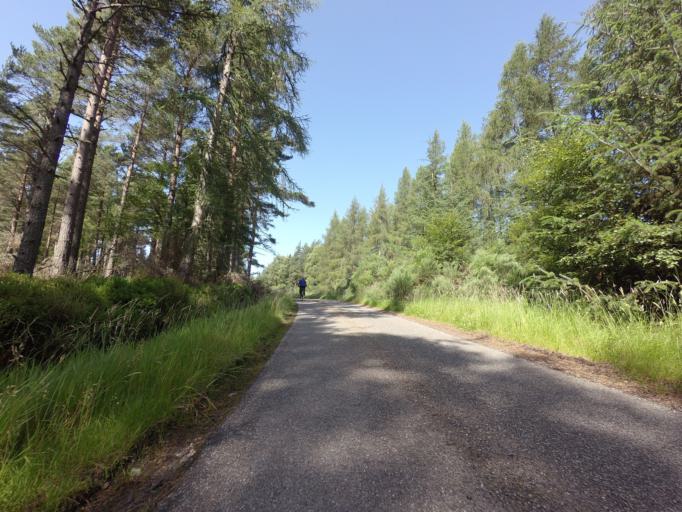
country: GB
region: Scotland
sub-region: Highland
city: Nairn
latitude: 57.4978
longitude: -3.9659
